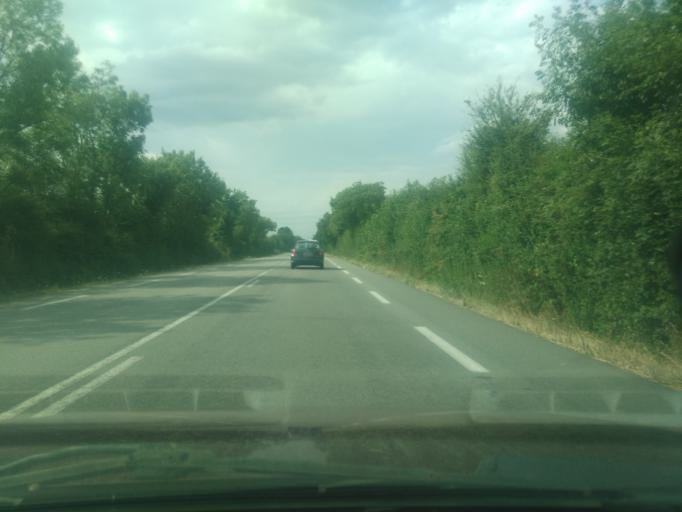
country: FR
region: Pays de la Loire
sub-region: Departement de la Vendee
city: Sainte-Cecile
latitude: 46.7644
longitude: -1.1053
